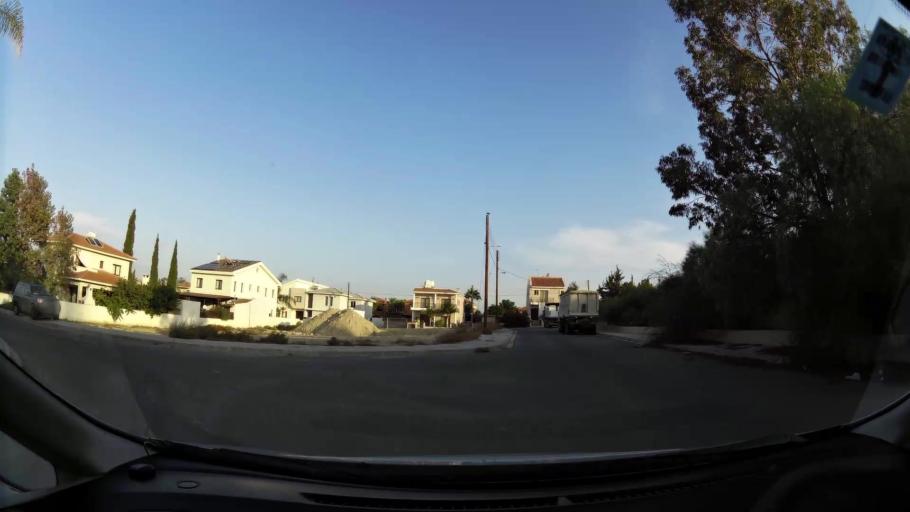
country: CY
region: Larnaka
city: Aradippou
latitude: 34.9261
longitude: 33.5953
